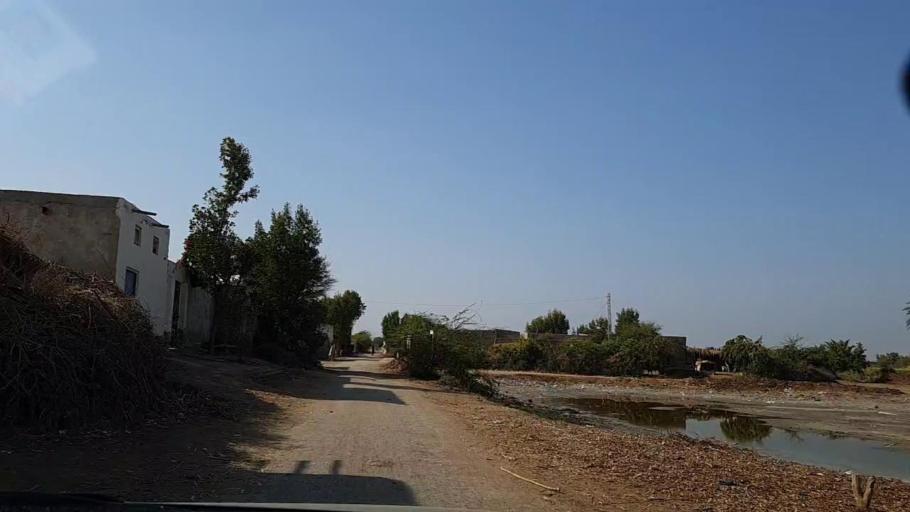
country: PK
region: Sindh
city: Digri
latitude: 25.1770
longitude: 69.0122
